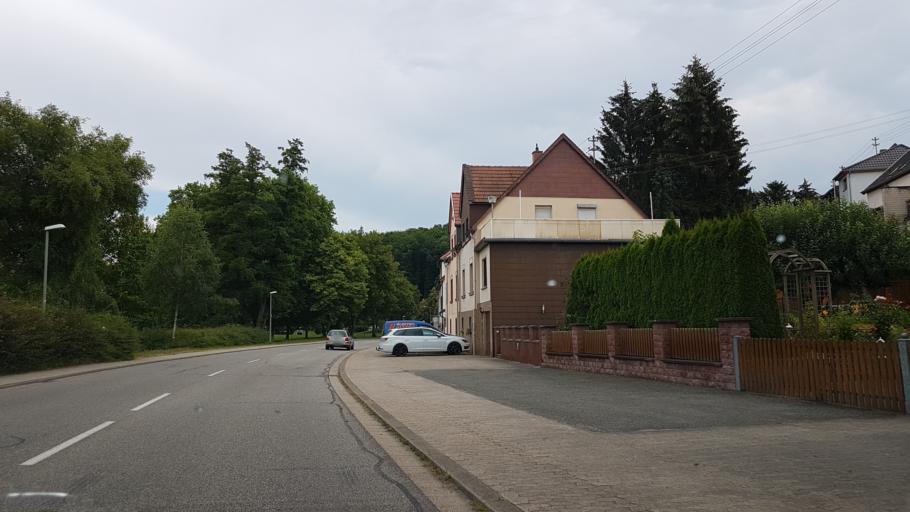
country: DE
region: Saarland
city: Quierschied
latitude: 49.3068
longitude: 7.0306
